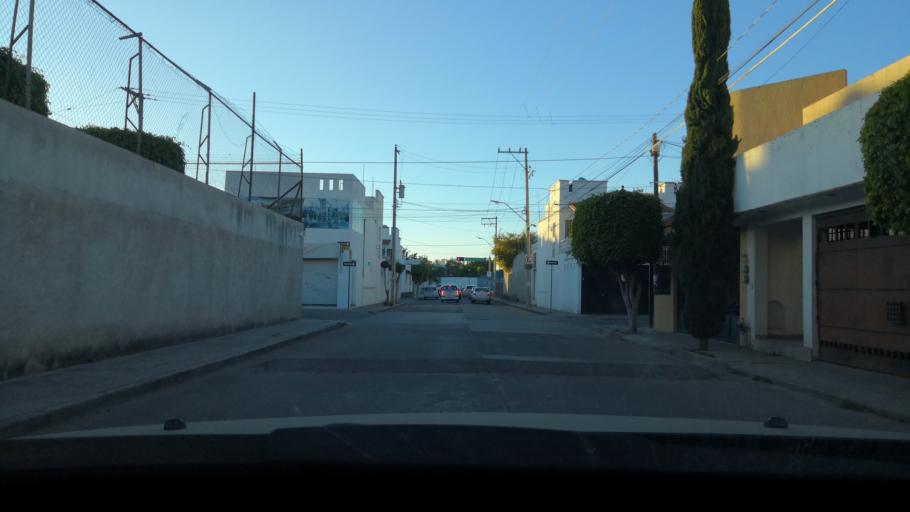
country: MX
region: Guanajuato
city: Leon
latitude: 21.1652
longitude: -101.6616
